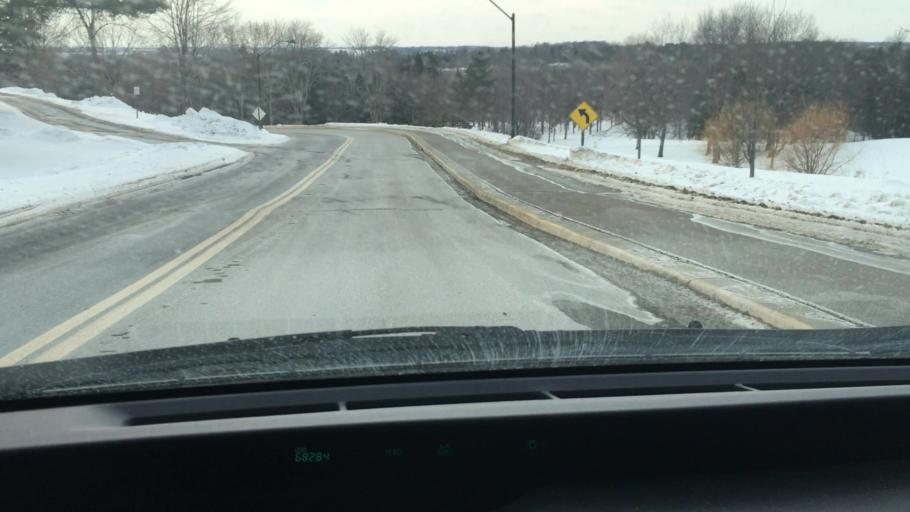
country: US
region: Minnesota
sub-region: Rice County
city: Northfield
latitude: 44.4597
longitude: -93.1866
